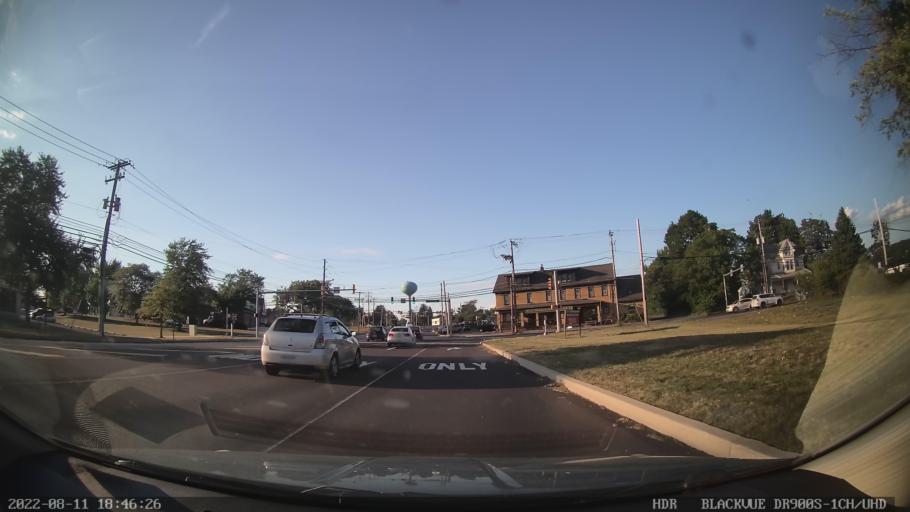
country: US
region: Pennsylvania
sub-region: Lehigh County
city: Wescosville
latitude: 40.5876
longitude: -75.5577
